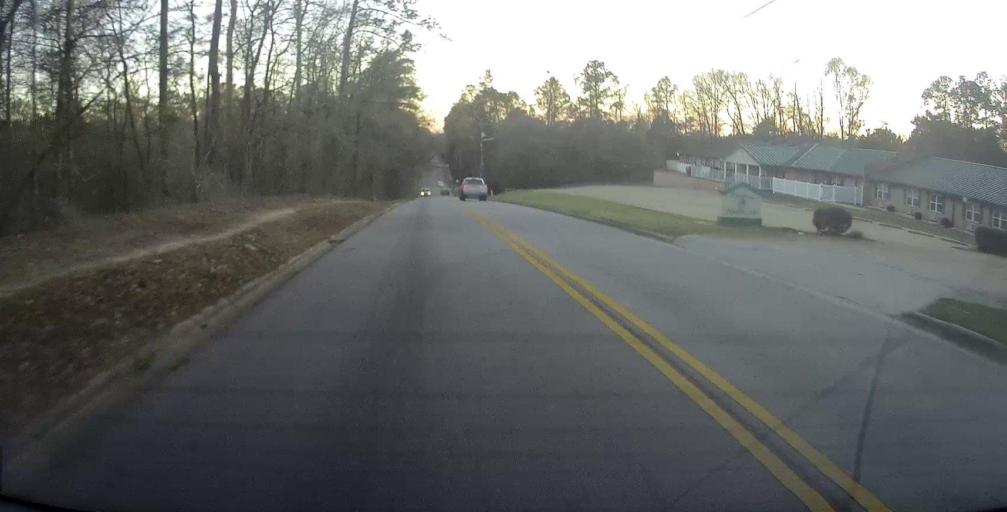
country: US
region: Alabama
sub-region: Russell County
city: Phenix City
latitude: 32.4914
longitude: -85.0187
